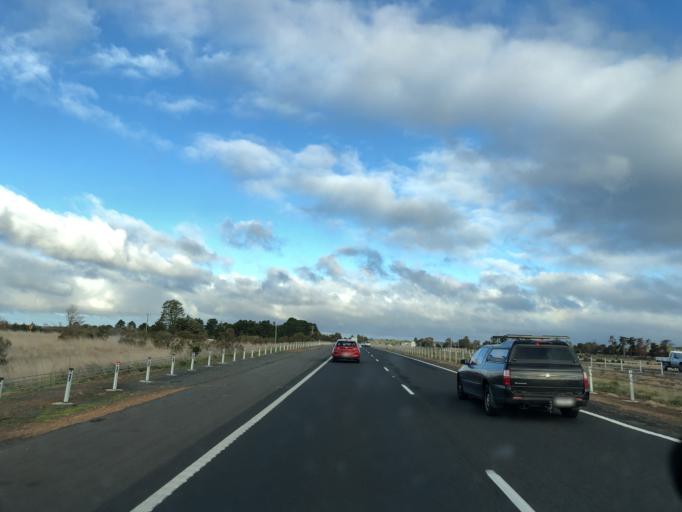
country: AU
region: Victoria
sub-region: Mount Alexander
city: Castlemaine
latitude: -37.2044
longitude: 144.4086
